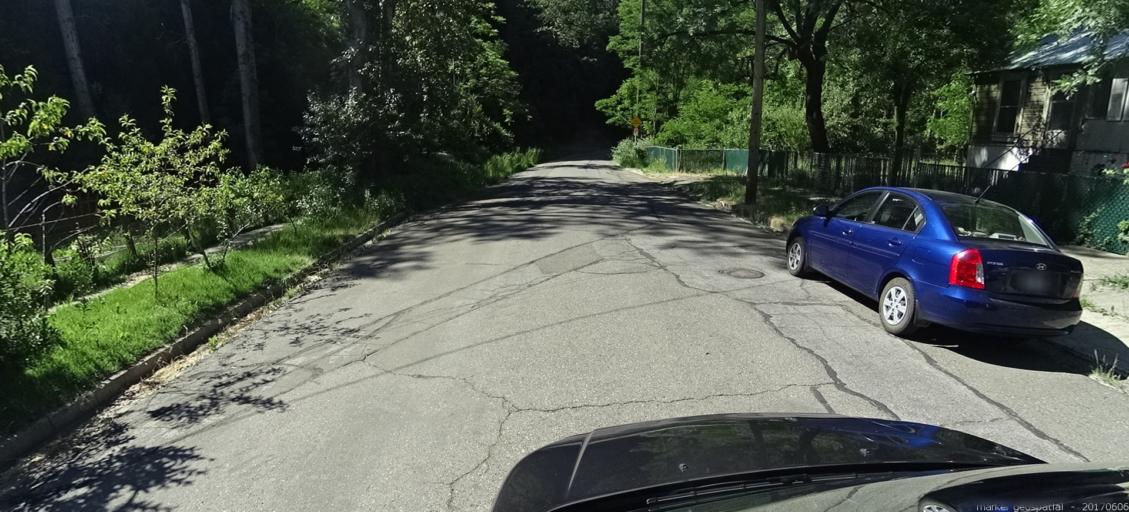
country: US
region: California
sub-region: Siskiyou County
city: Dunsmuir
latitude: 41.2057
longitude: -122.2705
